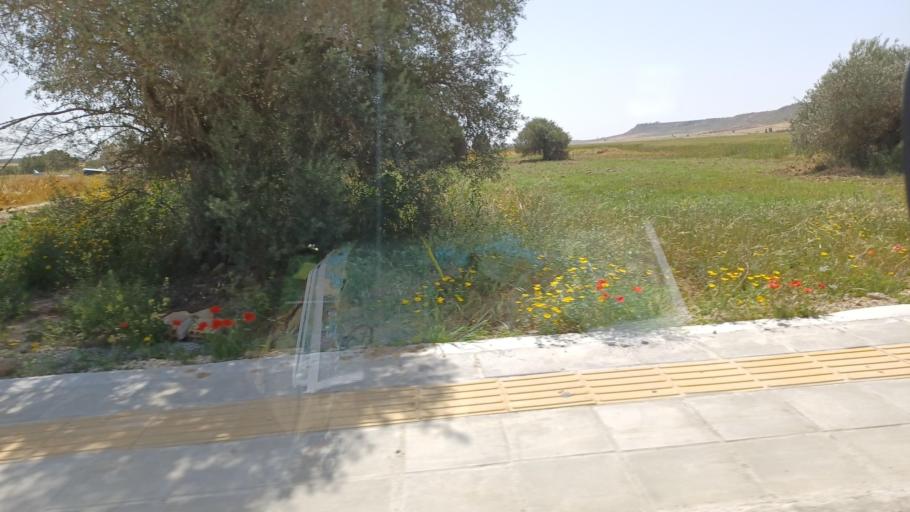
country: CY
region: Lefkosia
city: Mammari
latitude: 35.1833
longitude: 33.2099
